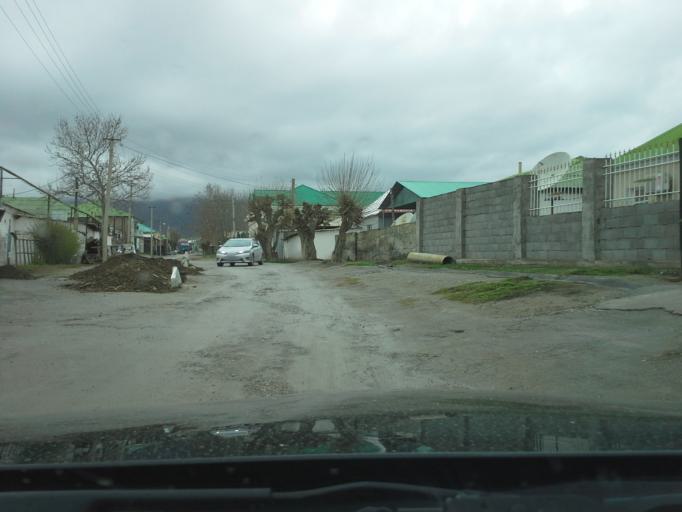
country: TM
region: Ahal
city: Abadan
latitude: 37.9615
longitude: 58.2209
